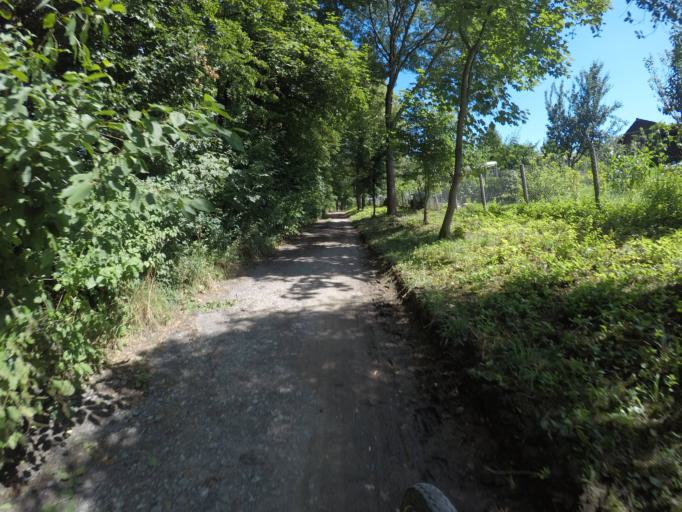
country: DE
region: Baden-Wuerttemberg
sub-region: Regierungsbezirk Stuttgart
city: Leinfelden-Echterdingen
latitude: 48.7164
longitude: 9.1654
